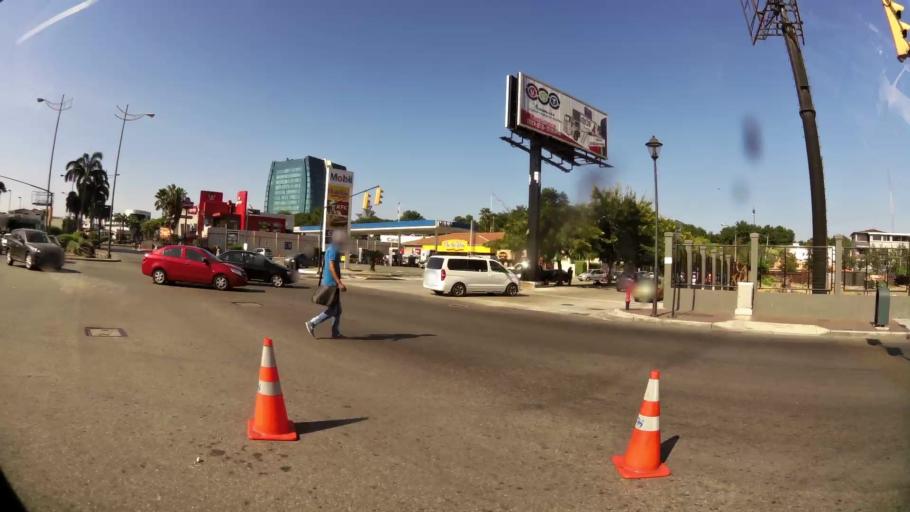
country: EC
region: Guayas
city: Guayaquil
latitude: -2.1641
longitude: -79.8968
